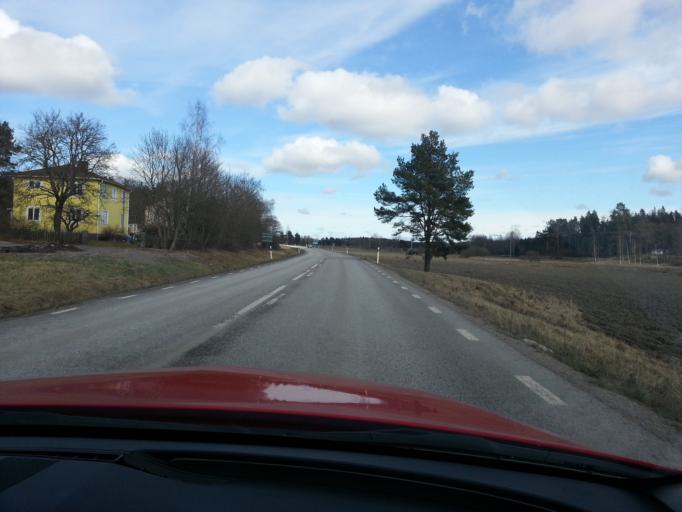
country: SE
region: Uppsala
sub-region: Osthammars Kommun
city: Gimo
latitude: 60.0636
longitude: 18.0831
